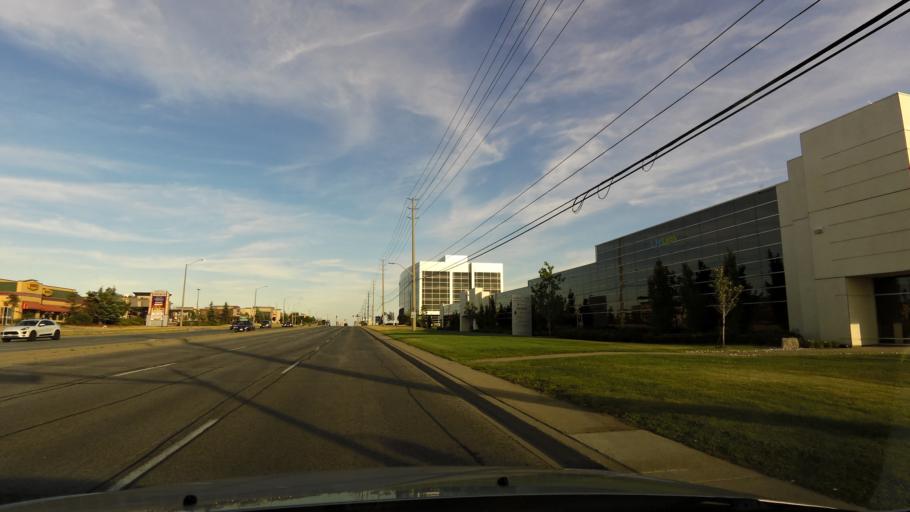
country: CA
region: Ontario
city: Mississauga
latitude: 43.6370
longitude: -79.6941
